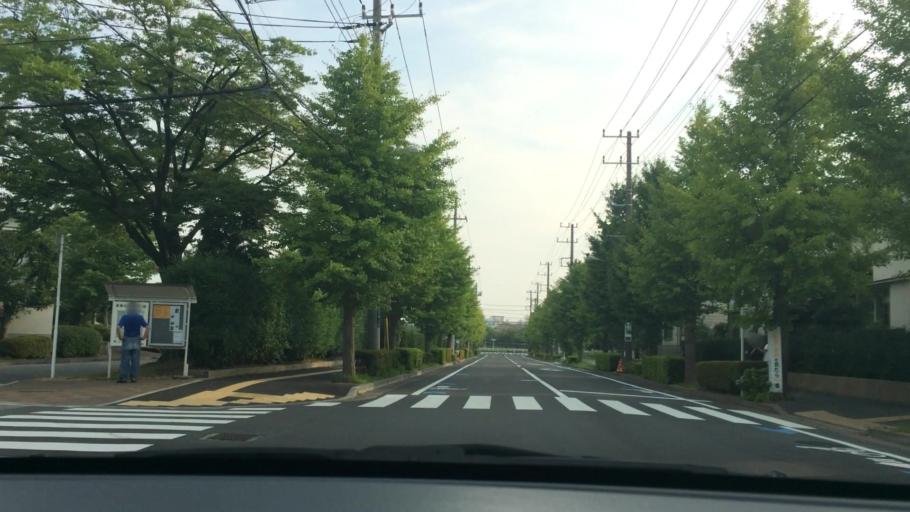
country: JP
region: Tokyo
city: Urayasu
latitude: 35.6382
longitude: 139.8933
